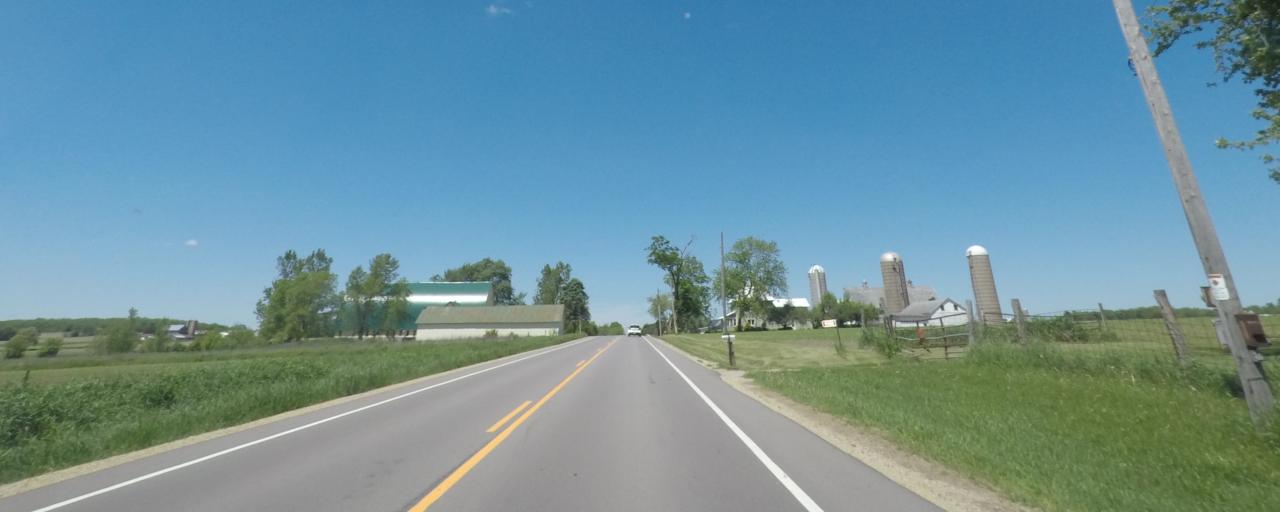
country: US
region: Wisconsin
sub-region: Green County
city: Brooklyn
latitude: 42.8148
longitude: -89.3692
